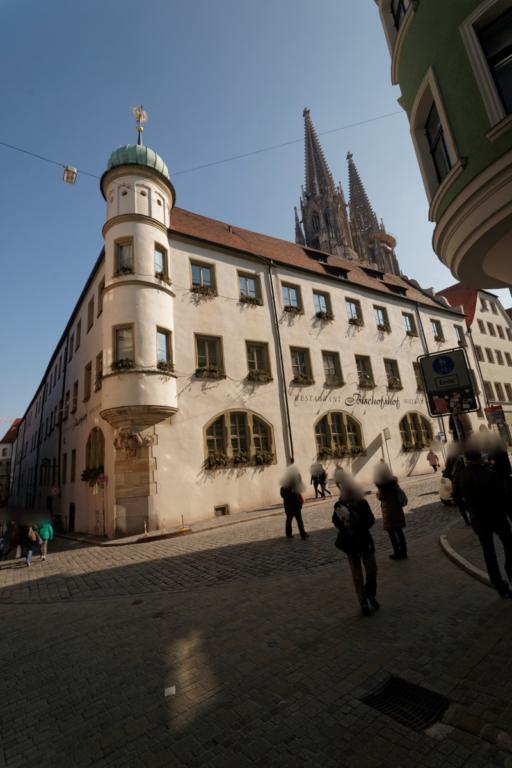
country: DE
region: Bavaria
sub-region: Upper Palatinate
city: Regensburg
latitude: 49.0203
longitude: 12.0973
